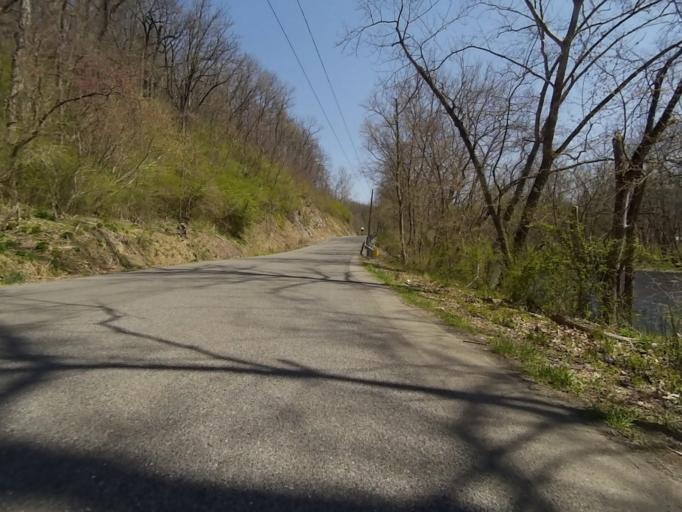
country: US
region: Pennsylvania
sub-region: Blair County
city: Williamsburg
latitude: 40.4761
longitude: -78.1960
